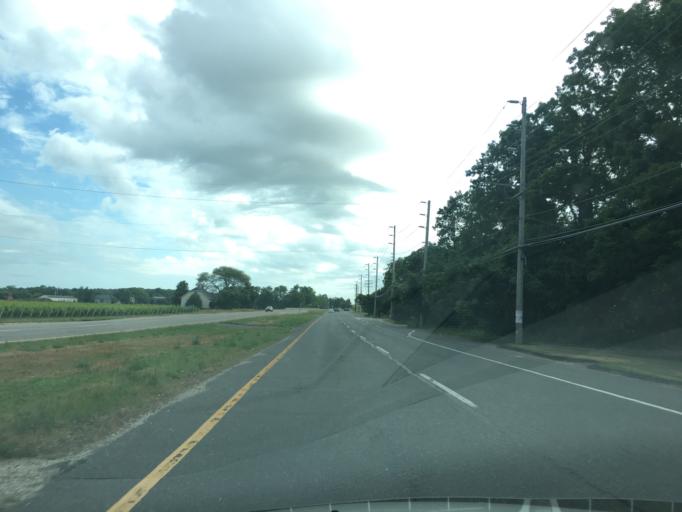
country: US
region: New York
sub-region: Suffolk County
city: Cutchogue
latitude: 41.0276
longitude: -72.4974
